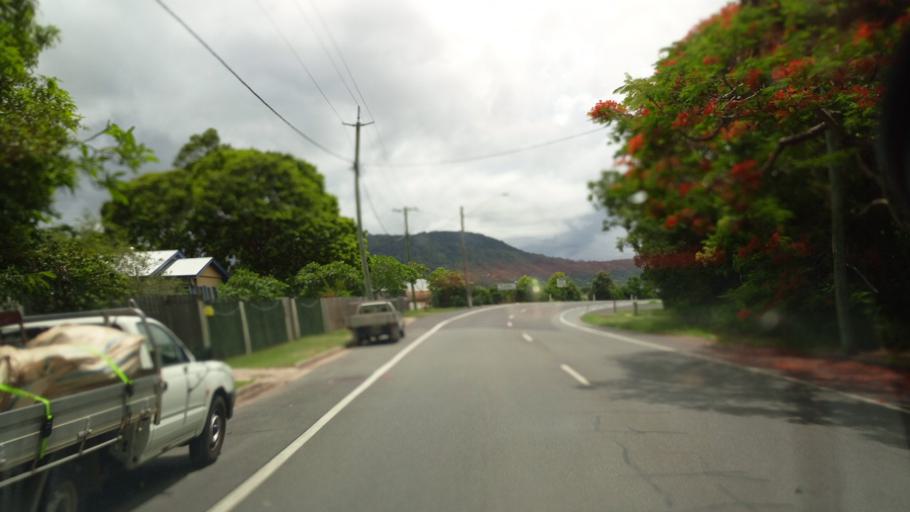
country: AU
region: Queensland
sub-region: Cairns
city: Redlynch
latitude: -16.8559
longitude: 145.7423
